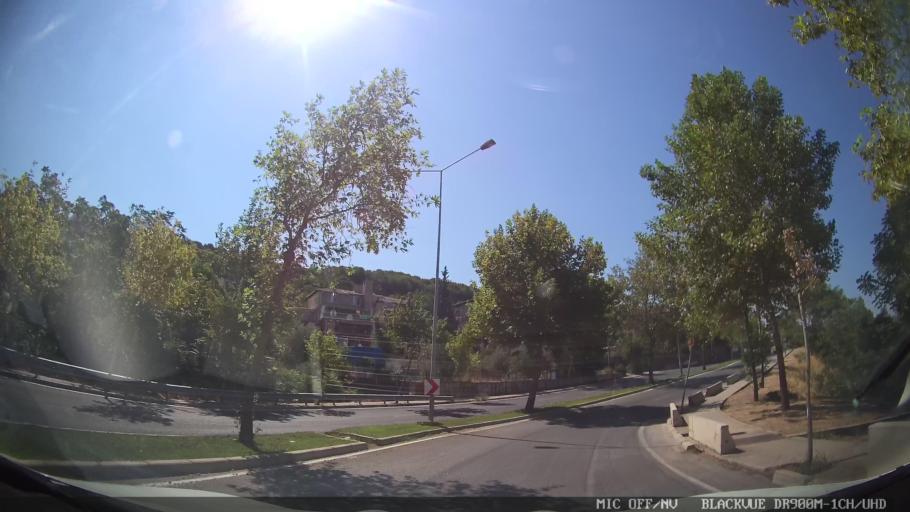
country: TR
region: Izmir
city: Karsiyaka
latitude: 38.5029
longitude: 27.0835
